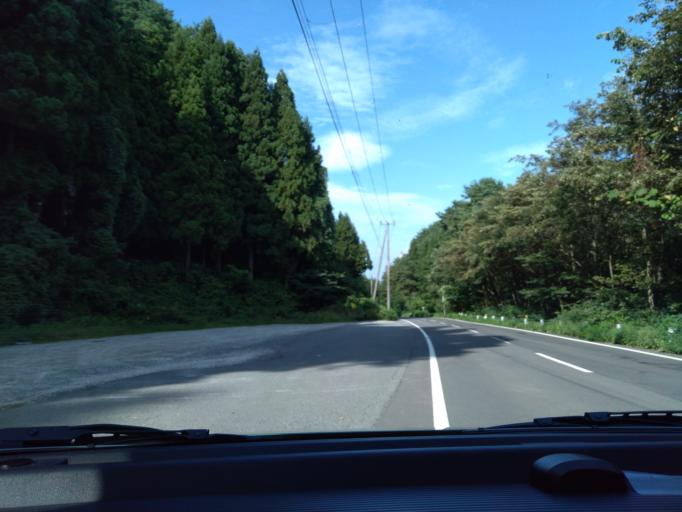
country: JP
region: Iwate
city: Morioka-shi
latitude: 39.6328
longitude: 141.0804
